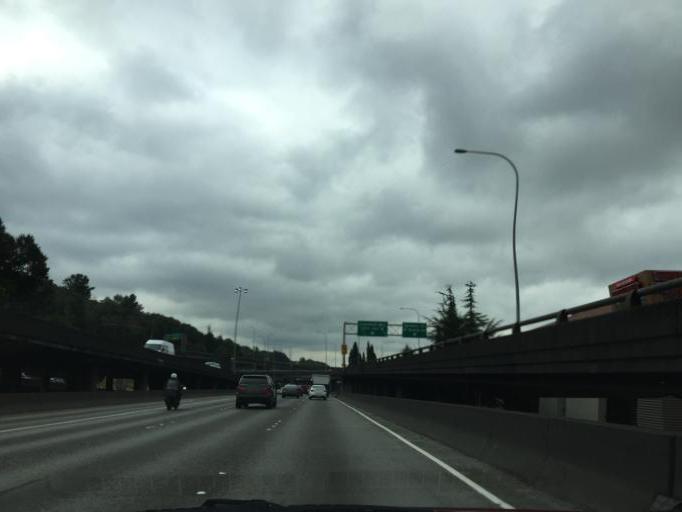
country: US
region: Washington
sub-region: King County
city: Seattle
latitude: 47.5753
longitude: -122.3200
